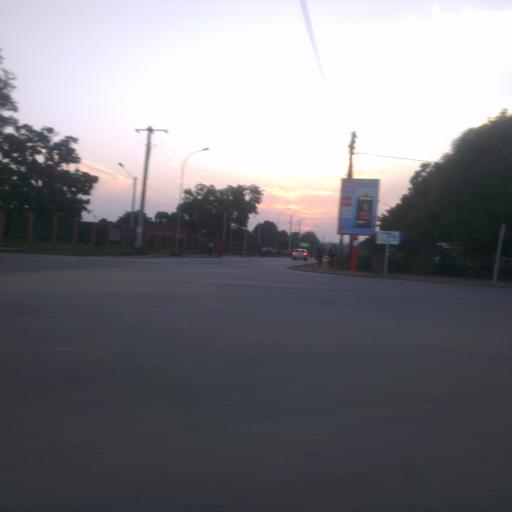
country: CI
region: Vallee du Bandama
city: Bouake
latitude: 7.6803
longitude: -5.0303
